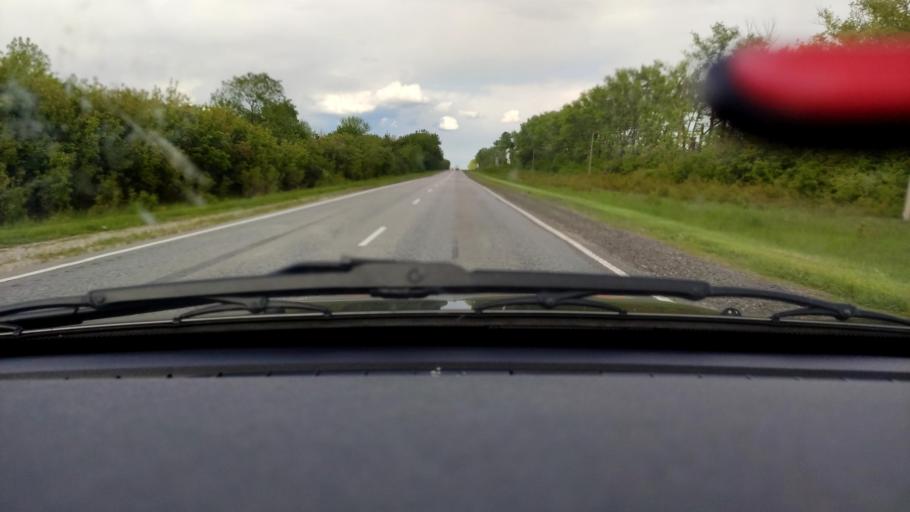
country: RU
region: Voronezj
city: Uryv-Pokrovka
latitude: 51.0804
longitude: 38.9990
